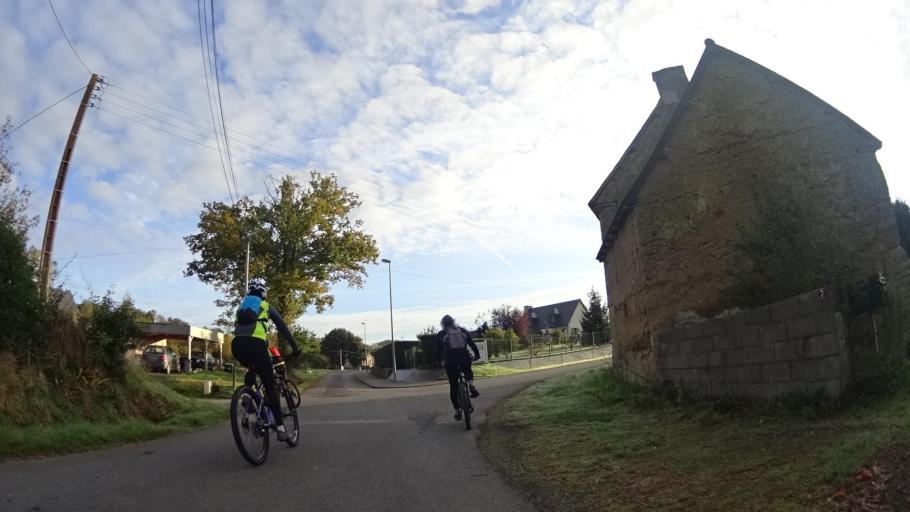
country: FR
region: Brittany
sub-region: Departement des Cotes-d'Armor
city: Evran
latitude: 48.3816
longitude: -1.9682
